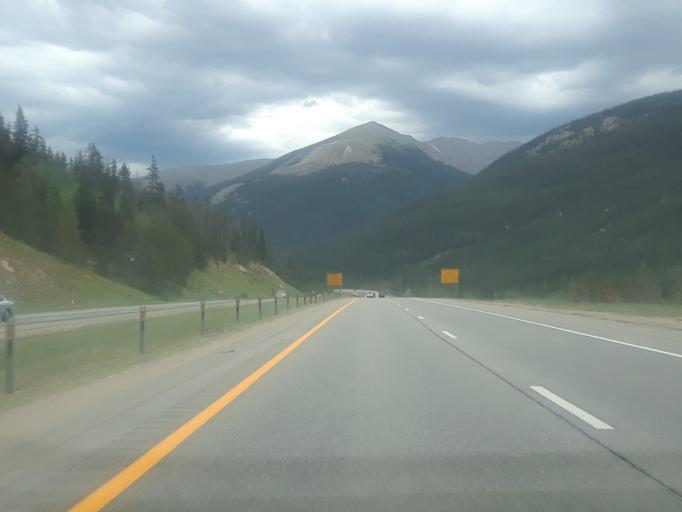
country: US
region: Colorado
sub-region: Clear Creek County
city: Georgetown
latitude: 39.6981
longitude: -105.8323
